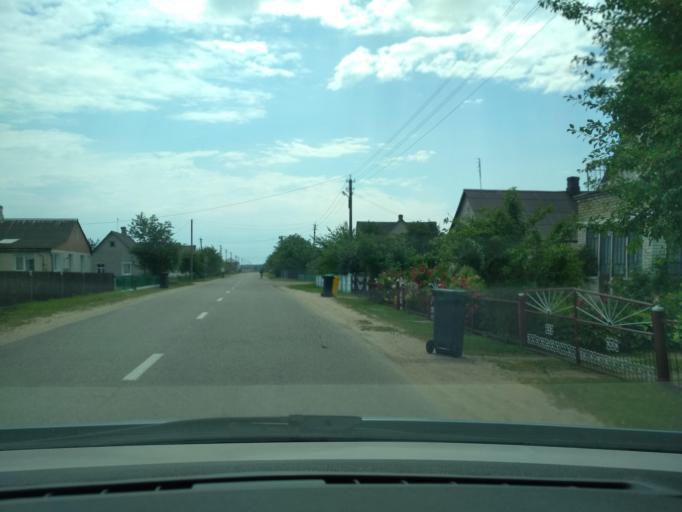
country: BY
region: Grodnenskaya
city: Astravyets
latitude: 54.6065
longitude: 25.9589
